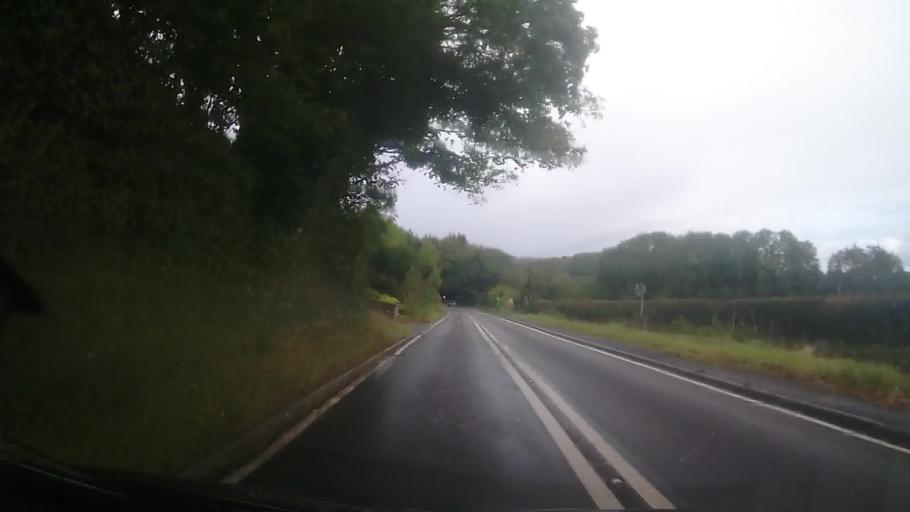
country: GB
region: England
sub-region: Shropshire
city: Much Wenlock
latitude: 52.6090
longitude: -2.5467
